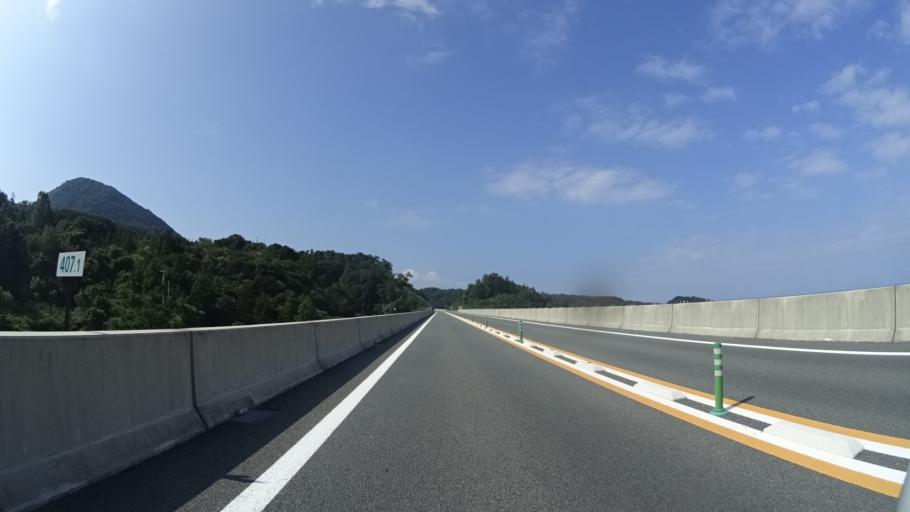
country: JP
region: Shimane
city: Odacho-oda
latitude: 35.1260
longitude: 132.3945
